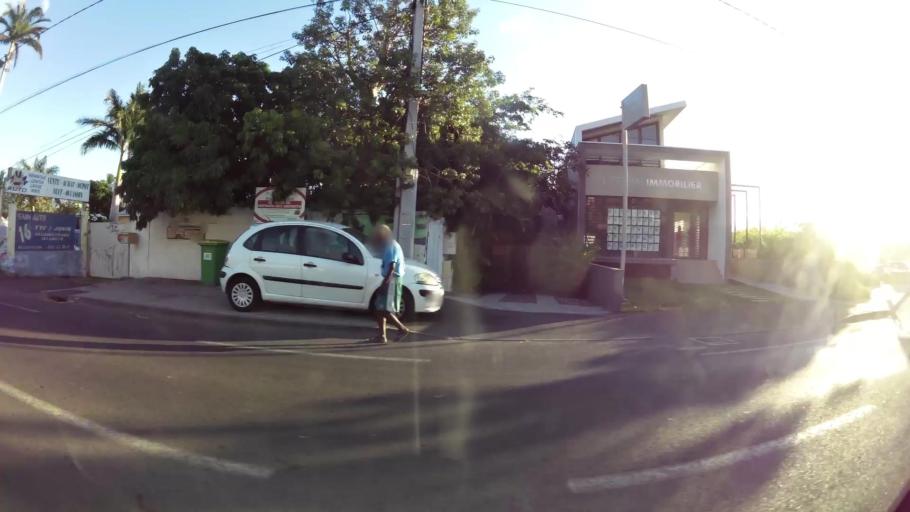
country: RE
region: Reunion
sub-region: Reunion
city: Trois-Bassins
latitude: -21.0810
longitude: 55.2300
